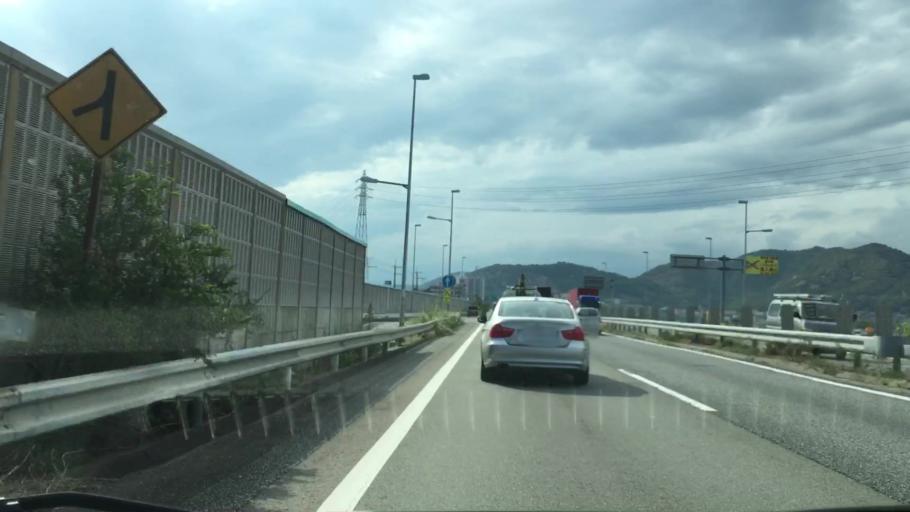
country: JP
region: Hyogo
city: Kakogawacho-honmachi
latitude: 34.7876
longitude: 134.8188
